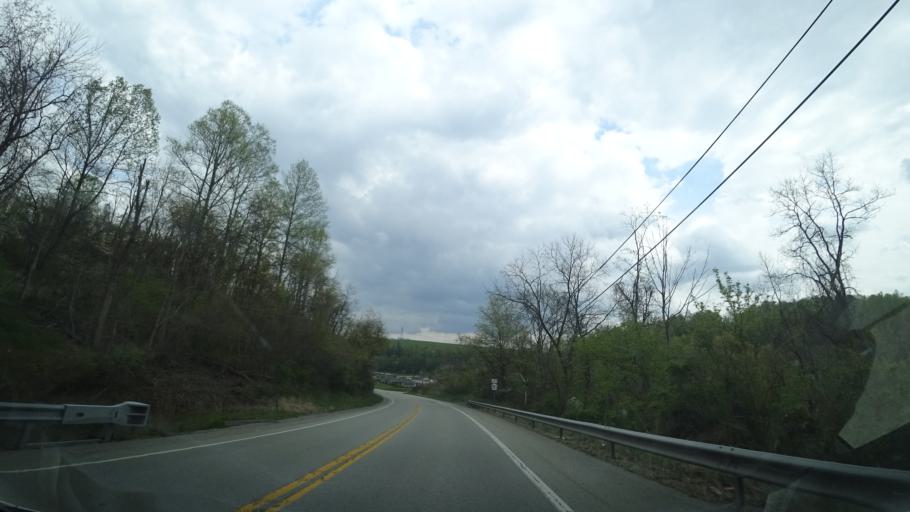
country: US
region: Pennsylvania
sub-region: Fayette County
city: Perryopolis
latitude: 40.0508
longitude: -79.7780
